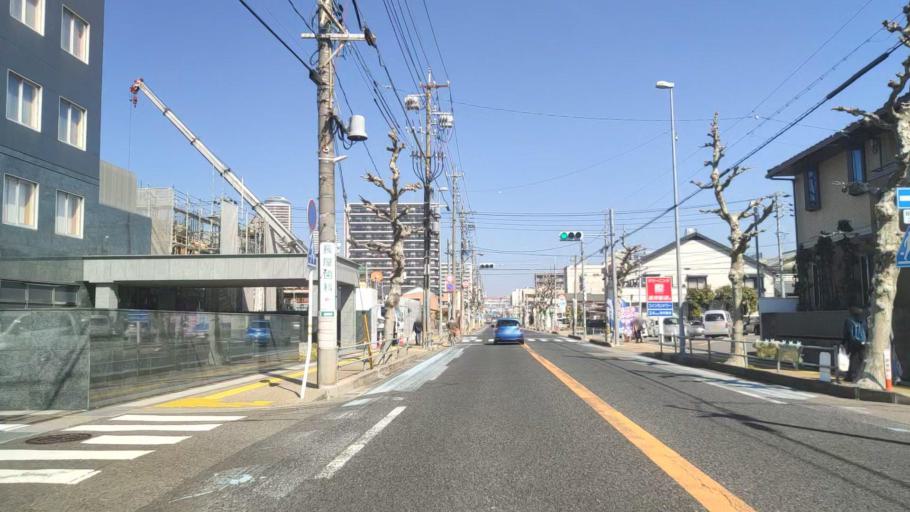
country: JP
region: Gifu
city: Gifu-shi
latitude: 35.4025
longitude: 136.7539
